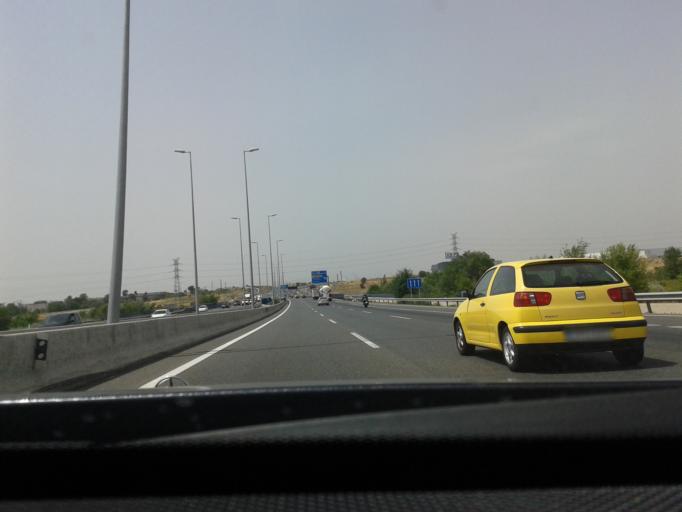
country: ES
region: Madrid
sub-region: Provincia de Madrid
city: Torrejon de Ardoz
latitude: 40.4728
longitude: -3.4197
